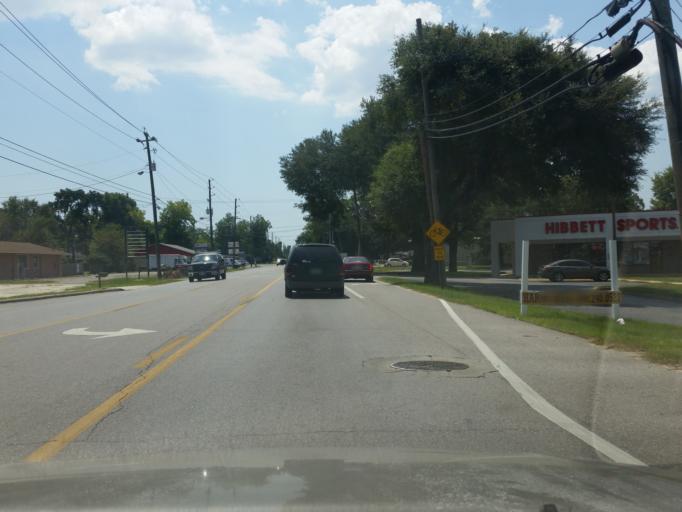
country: US
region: Florida
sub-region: Escambia County
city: Ensley
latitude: 30.5324
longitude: -87.2734
